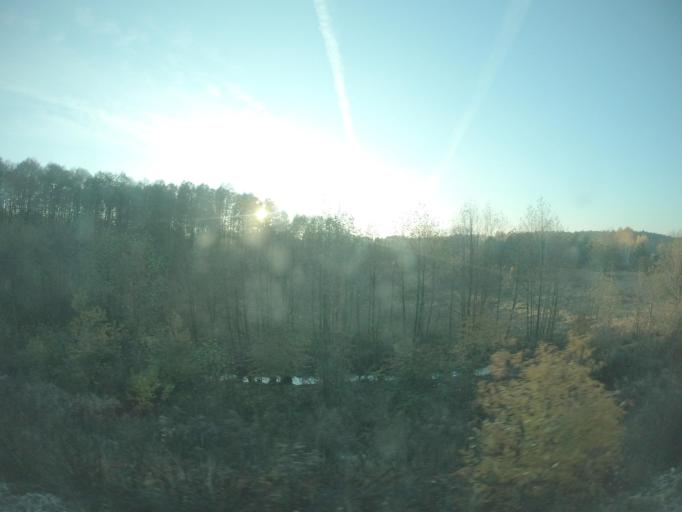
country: PL
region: Lubusz
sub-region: Powiat slubicki
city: Rzepin
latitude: 52.3364
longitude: 14.8327
